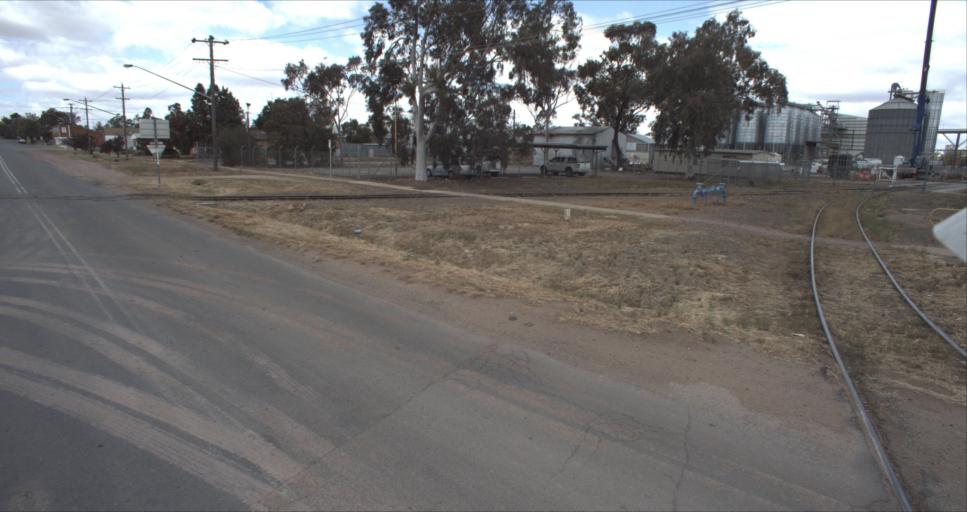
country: AU
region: New South Wales
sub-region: Leeton
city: Leeton
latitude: -34.5548
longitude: 146.3965
